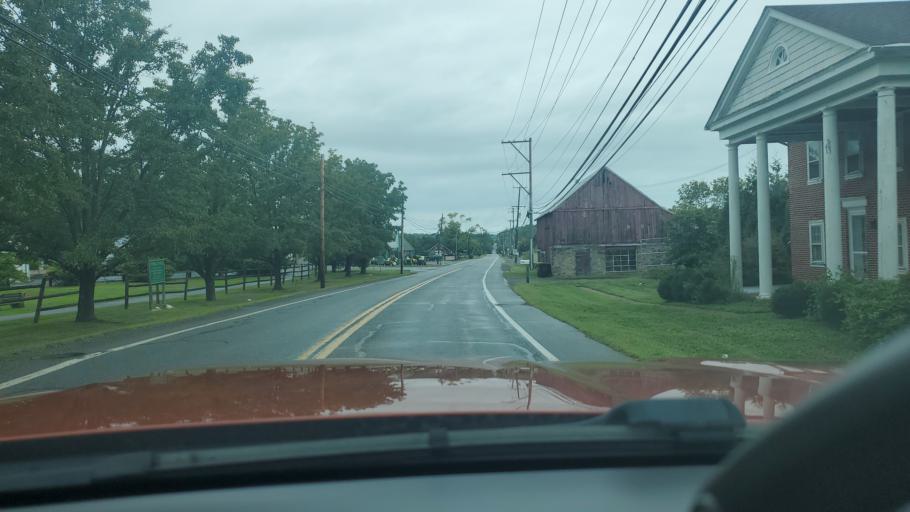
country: US
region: Pennsylvania
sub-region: Montgomery County
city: Spring Mount
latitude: 40.2799
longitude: -75.4809
